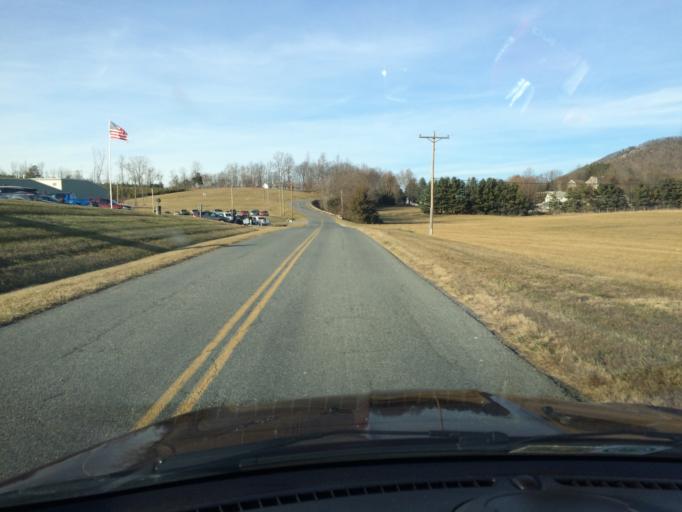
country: US
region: Virginia
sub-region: Botetourt County
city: Fincastle
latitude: 37.6089
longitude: -79.8412
